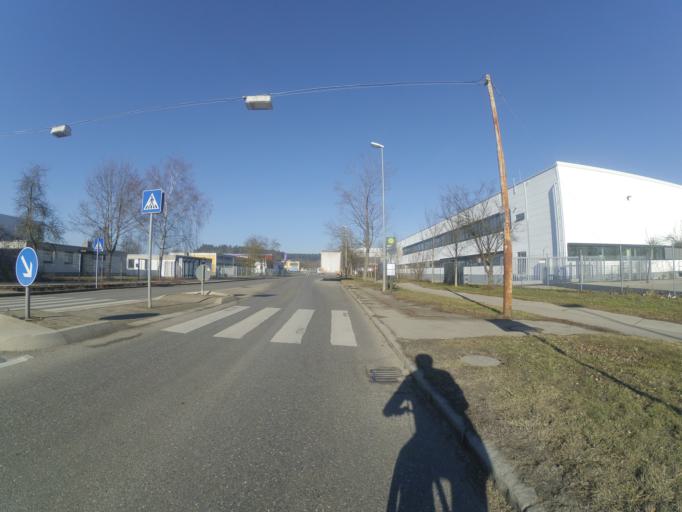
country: DE
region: Baden-Wuerttemberg
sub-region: Tuebingen Region
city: Erbach
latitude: 48.3600
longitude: 9.9387
